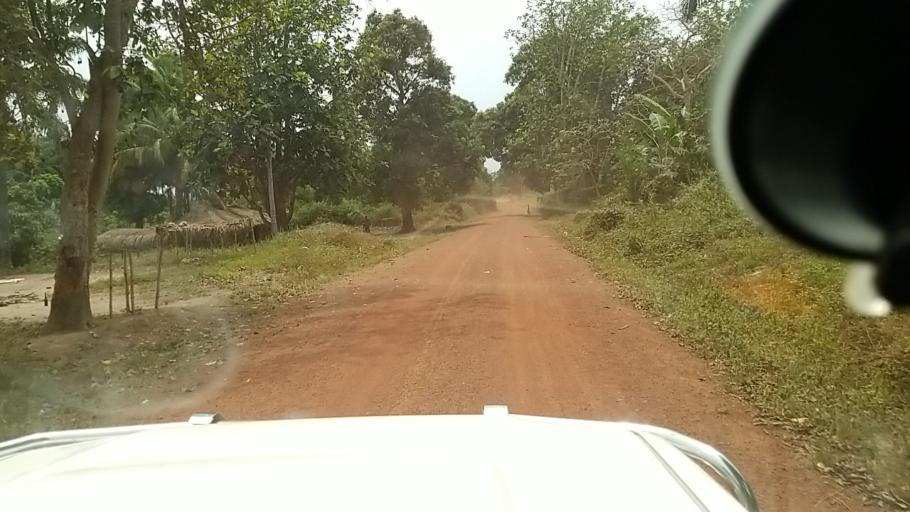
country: CD
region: Equateur
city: Libenge
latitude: 3.7316
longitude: 18.7750
